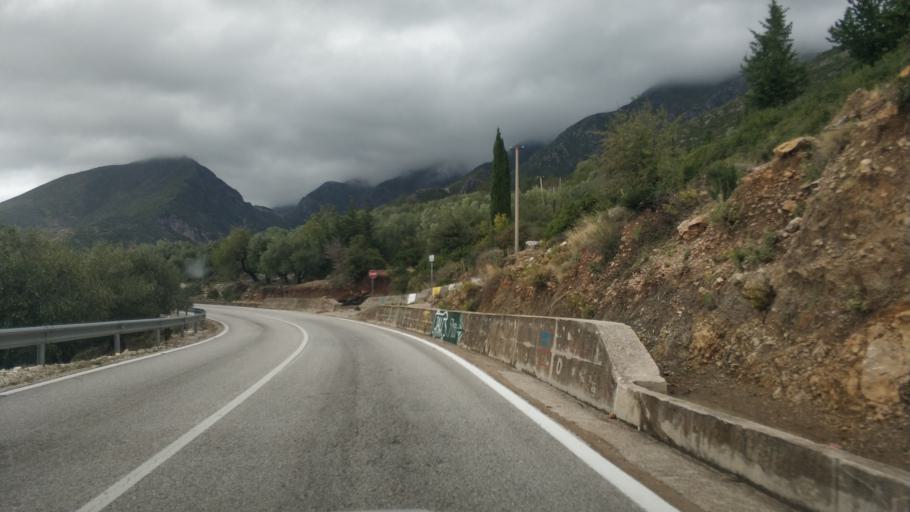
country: AL
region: Vlore
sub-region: Rrethi i Vlores
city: Vranisht
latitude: 40.1452
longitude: 19.6849
